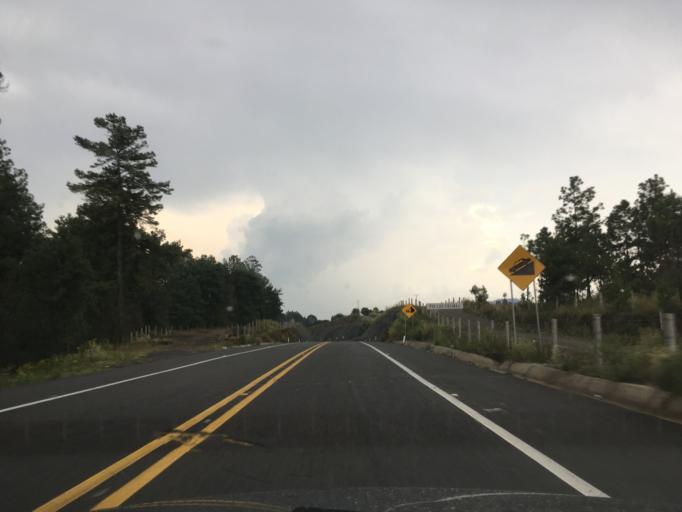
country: MX
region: Michoacan
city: Angahuan
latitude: 19.5112
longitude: -102.1648
